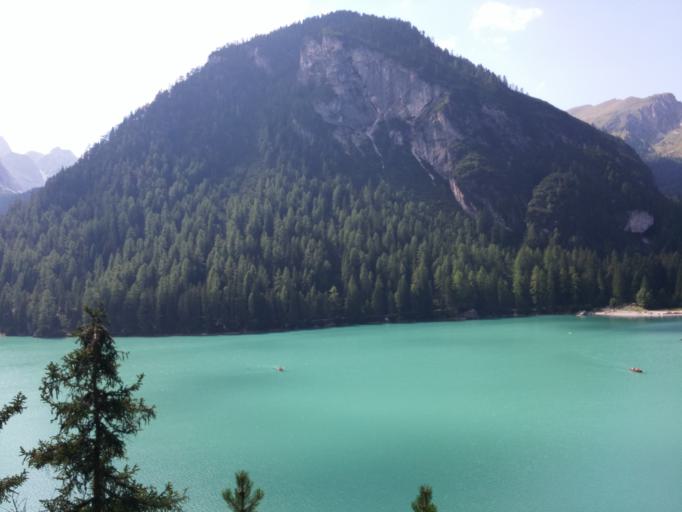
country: IT
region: Trentino-Alto Adige
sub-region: Bolzano
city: Braies
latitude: 46.6948
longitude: 12.0887
